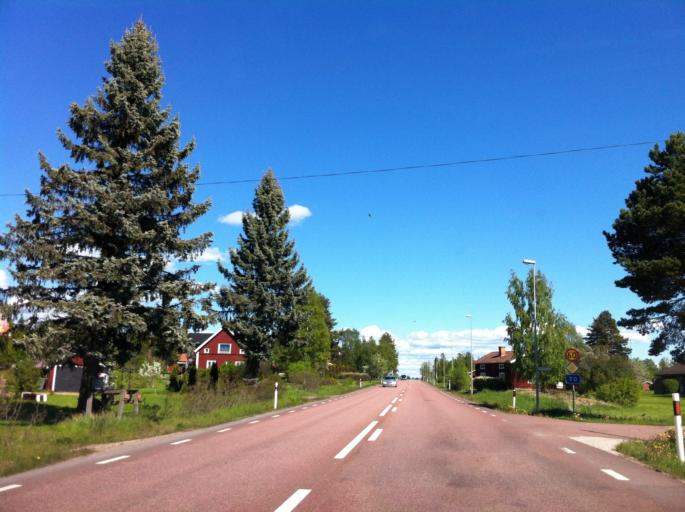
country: SE
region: Dalarna
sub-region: Leksand Municipality
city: Siljansnas
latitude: 60.9275
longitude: 14.8027
